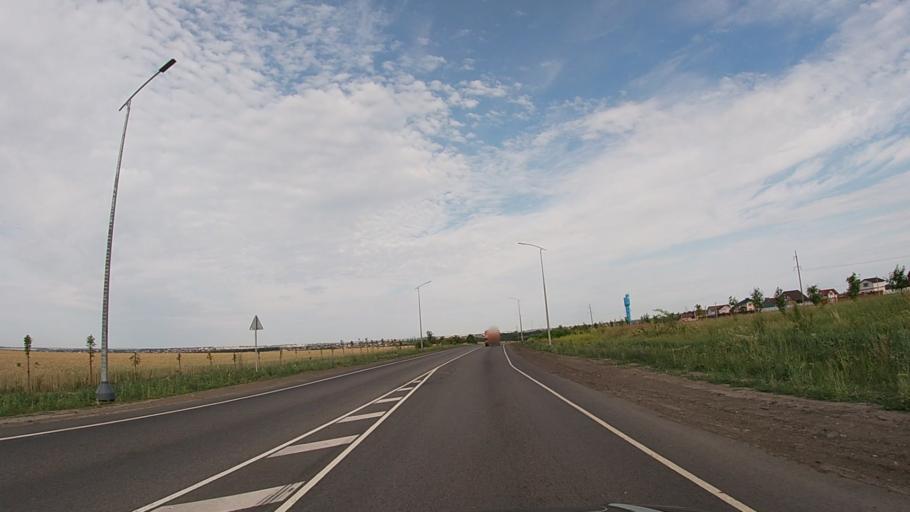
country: RU
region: Belgorod
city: Severnyy
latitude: 50.6653
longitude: 36.5022
